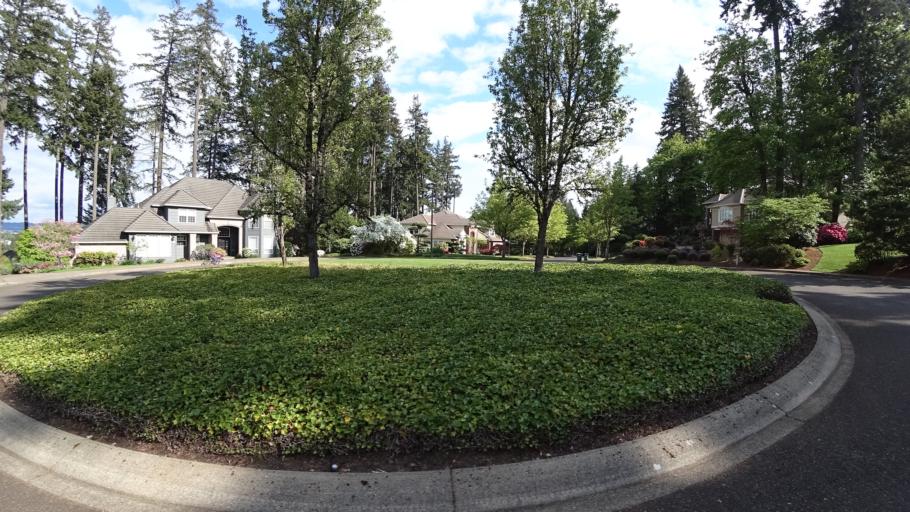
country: US
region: Oregon
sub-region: Washington County
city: Beaverton
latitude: 45.4466
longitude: -122.8382
